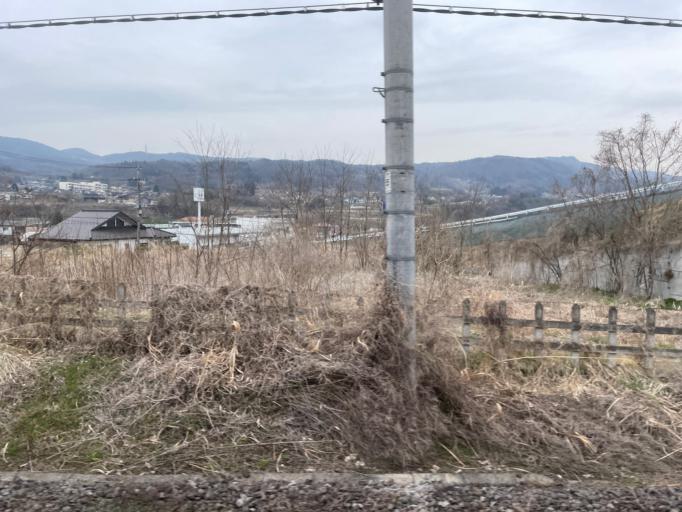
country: JP
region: Gunma
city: Numata
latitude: 36.6348
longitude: 139.0402
